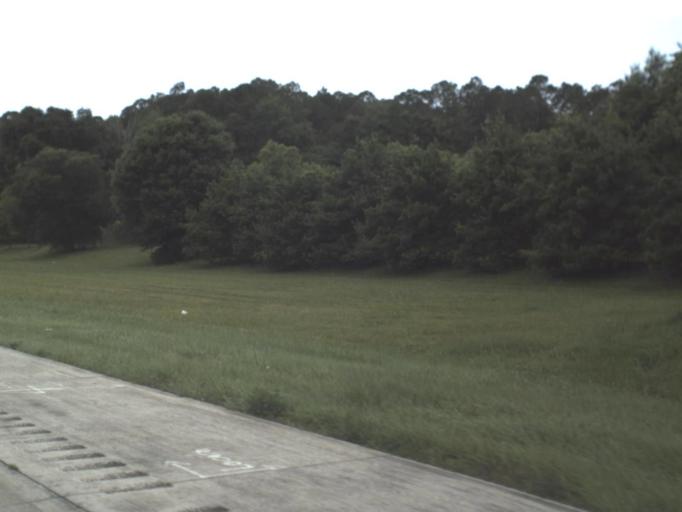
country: US
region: Florida
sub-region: Saint Johns County
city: Fruit Cove
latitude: 30.1709
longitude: -81.5308
